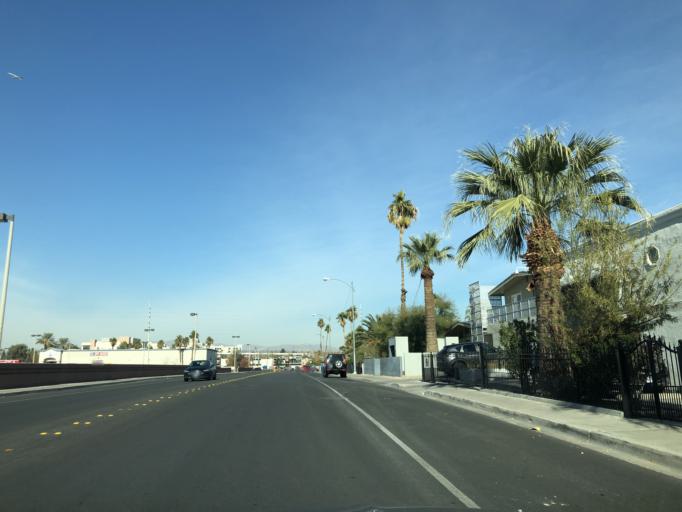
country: US
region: Nevada
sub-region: Clark County
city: Winchester
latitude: 36.1272
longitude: -115.1346
